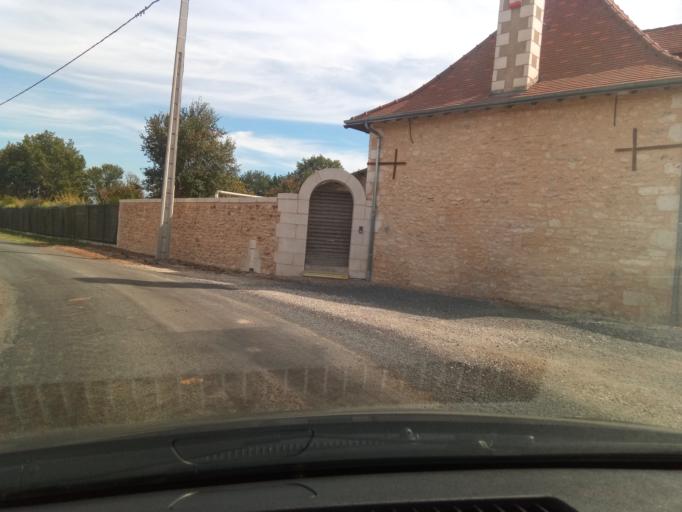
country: FR
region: Poitou-Charentes
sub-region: Departement de la Vienne
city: Chauvigny
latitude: 46.5547
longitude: 0.7395
